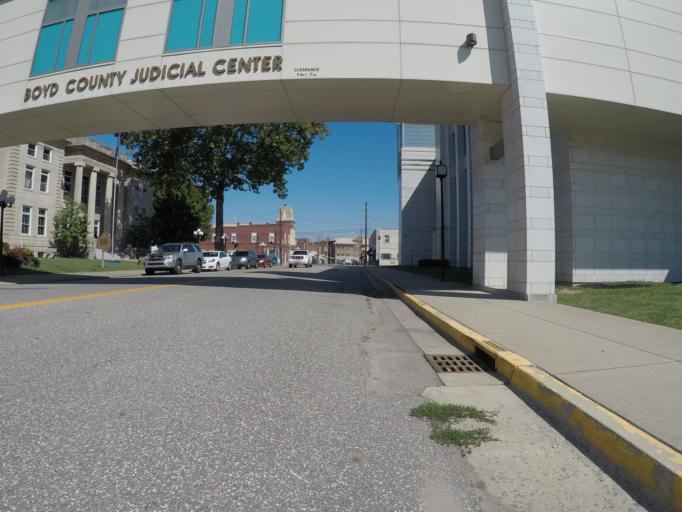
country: US
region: Kentucky
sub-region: Boyd County
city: Catlettsburg
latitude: 38.4152
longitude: -82.5980
